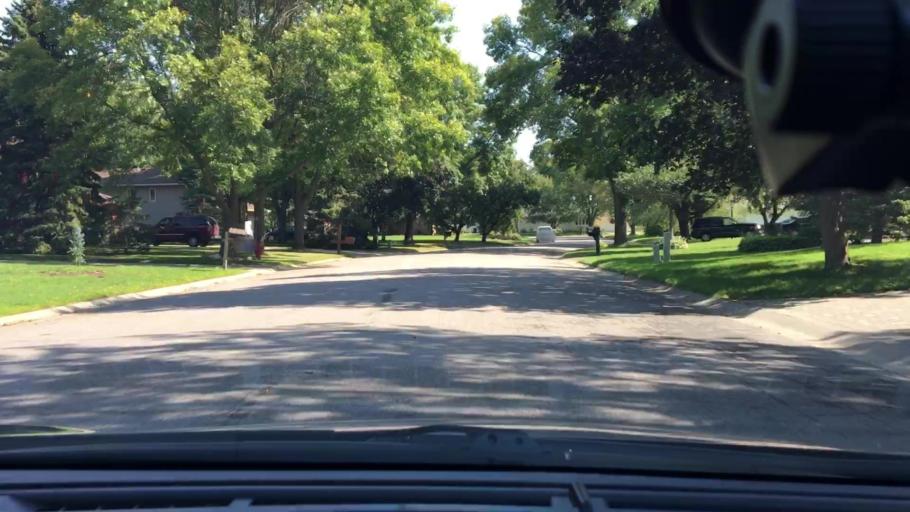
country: US
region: Minnesota
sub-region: Wright County
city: Saint Michael
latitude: 45.2024
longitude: -93.6681
